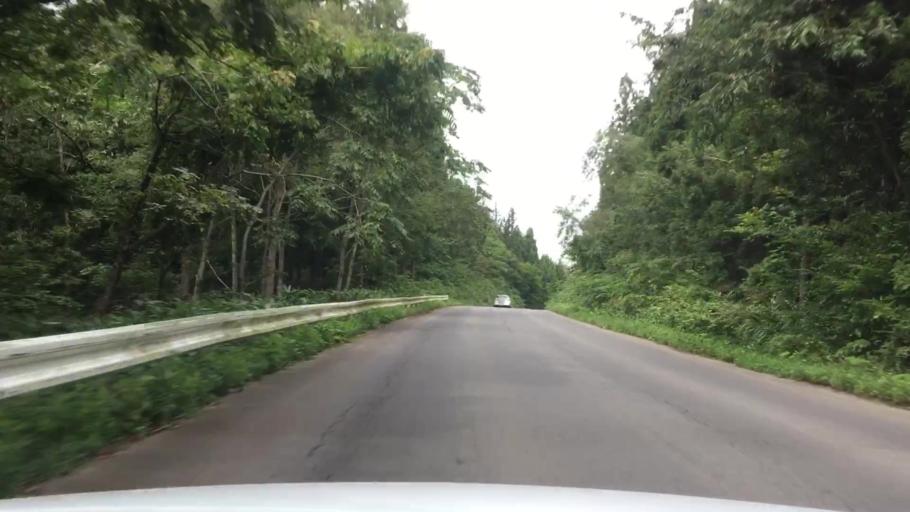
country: JP
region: Aomori
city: Shimokizukuri
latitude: 40.7156
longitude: 140.2612
